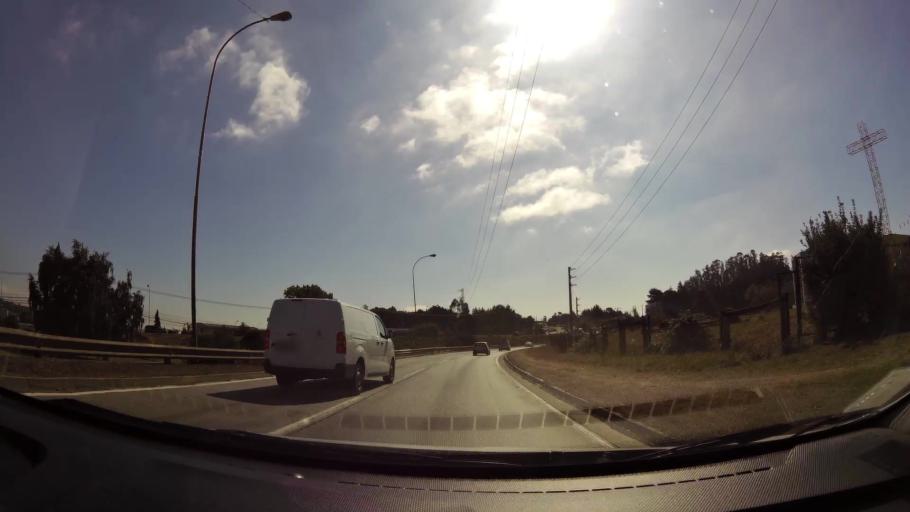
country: CL
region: Biobio
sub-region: Provincia de Concepcion
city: Concepcion
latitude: -36.7995
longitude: -73.0565
